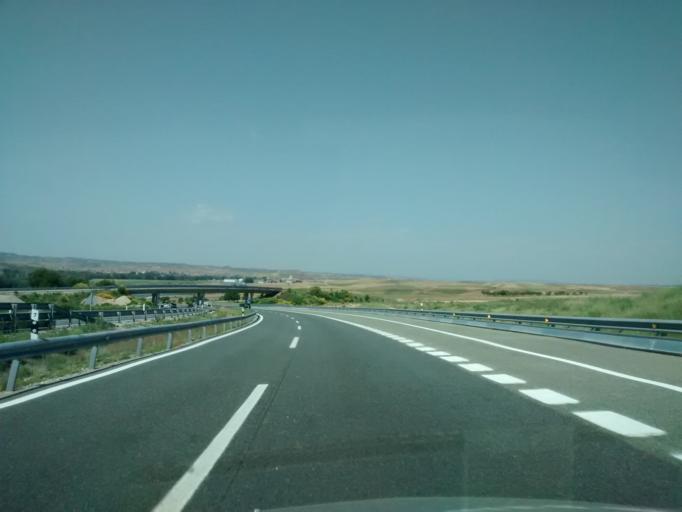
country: ES
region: Aragon
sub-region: Provincia de Zaragoza
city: Contamina
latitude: 41.3100
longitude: -1.9216
